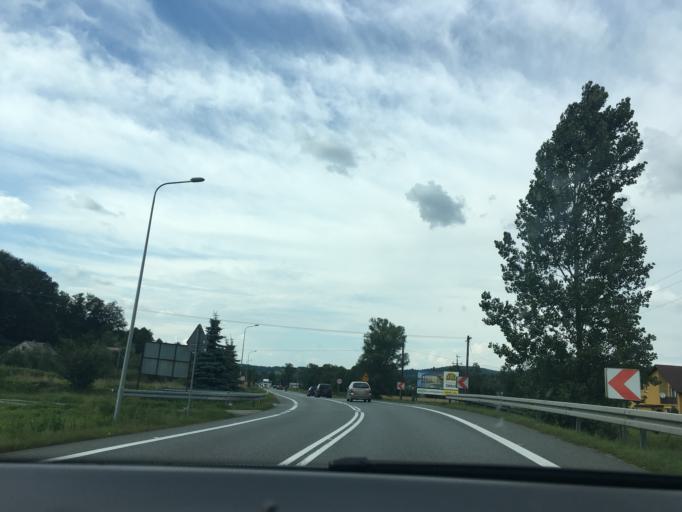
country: PL
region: Subcarpathian Voivodeship
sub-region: Powiat strzyzowski
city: Niebylec
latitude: 49.8761
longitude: 21.9054
